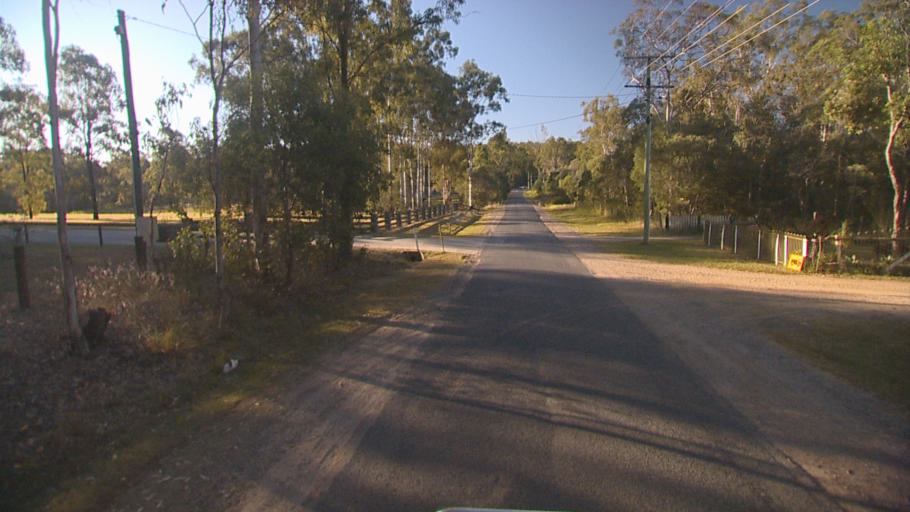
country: AU
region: Queensland
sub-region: Logan
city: Chambers Flat
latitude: -27.7715
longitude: 153.1296
